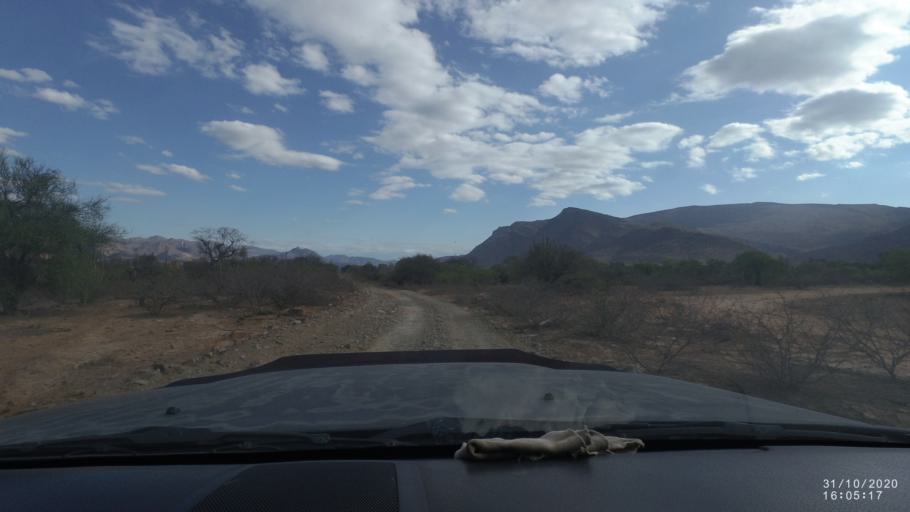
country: BO
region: Chuquisaca
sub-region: Provincia Zudanez
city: Mojocoya
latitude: -18.3653
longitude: -64.6497
